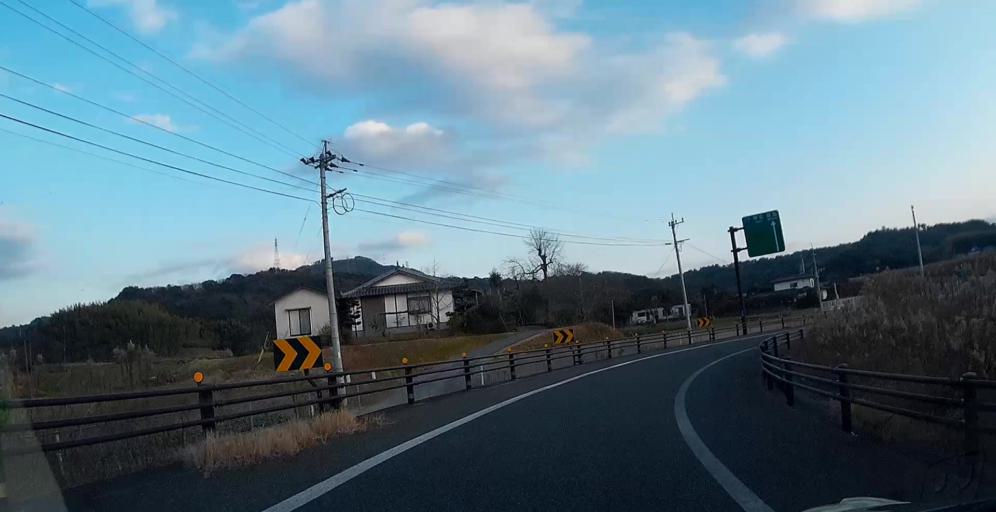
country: JP
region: Kumamoto
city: Kumamoto
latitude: 32.7448
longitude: 130.8028
